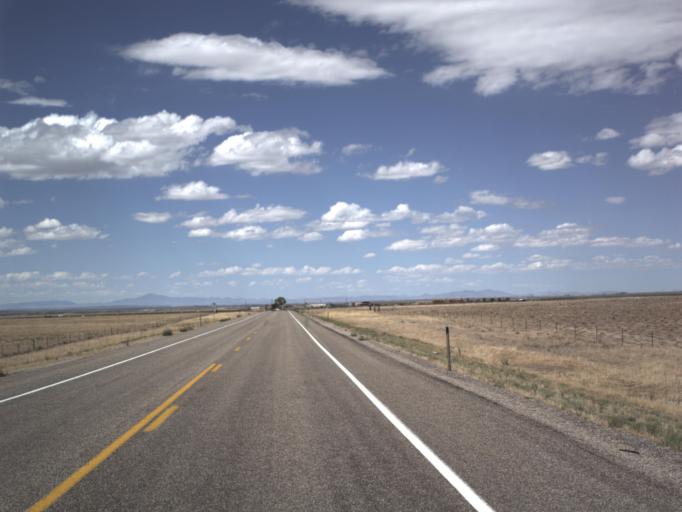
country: US
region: Utah
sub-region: Millard County
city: Fillmore
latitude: 39.1147
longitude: -112.3069
